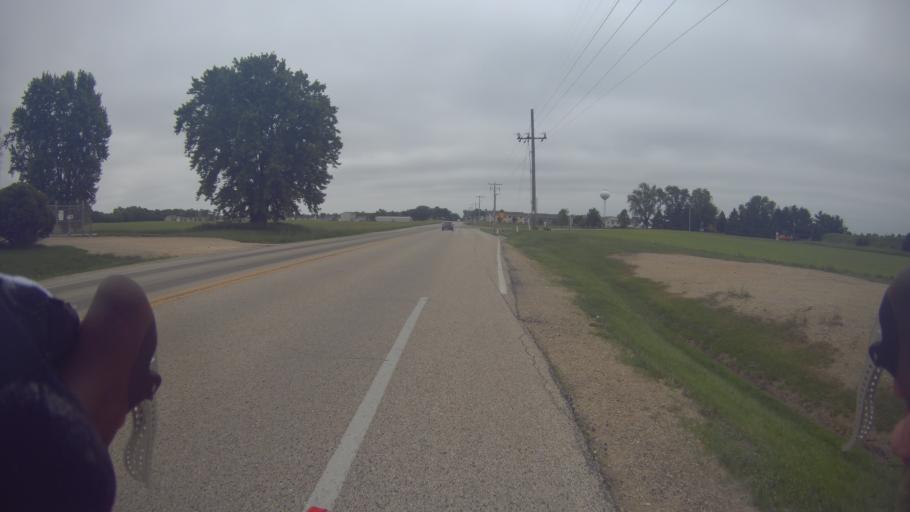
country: US
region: Wisconsin
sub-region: Green County
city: Brooklyn
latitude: 42.8637
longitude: -89.3692
